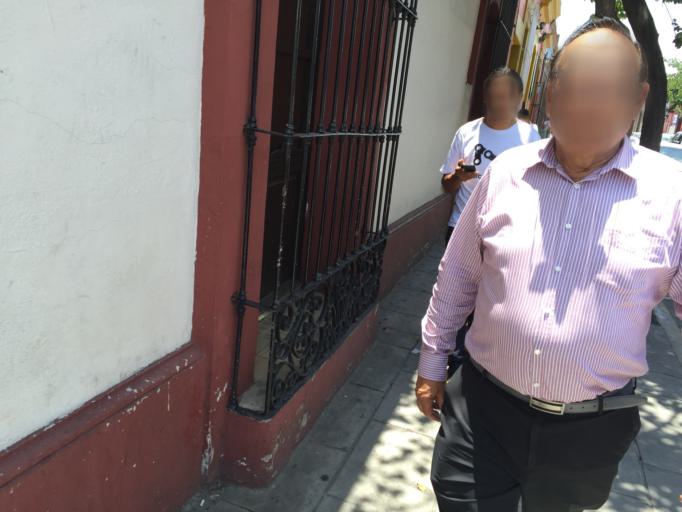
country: MX
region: Oaxaca
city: Oaxaca de Juarez
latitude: 17.0612
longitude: -96.7210
